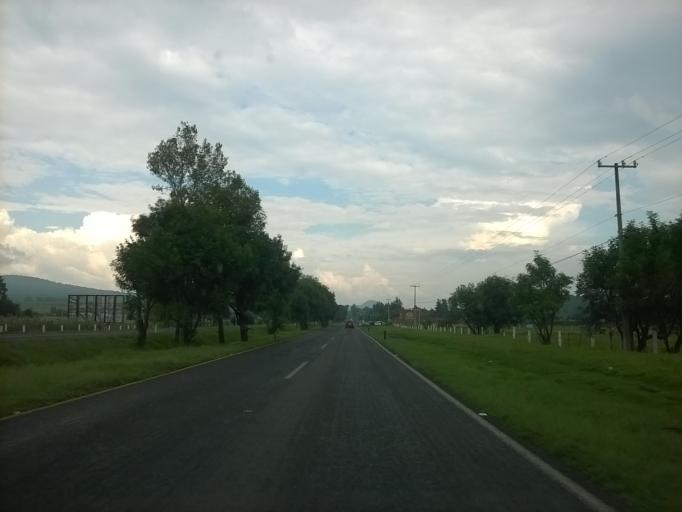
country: MX
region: Michoacan
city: Cuanajo
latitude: 19.5363
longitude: -101.5172
